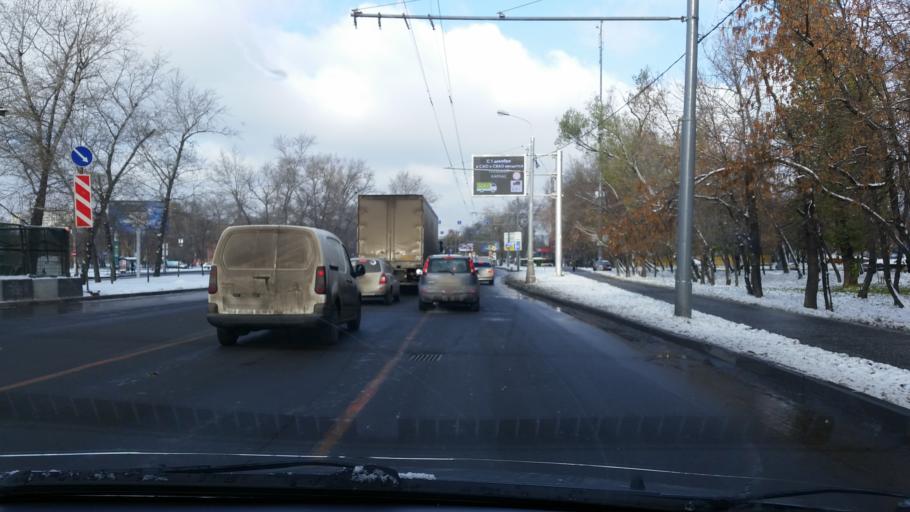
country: RU
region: Moskovskaya
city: Vostochnoe Degunino
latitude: 55.8766
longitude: 37.5474
